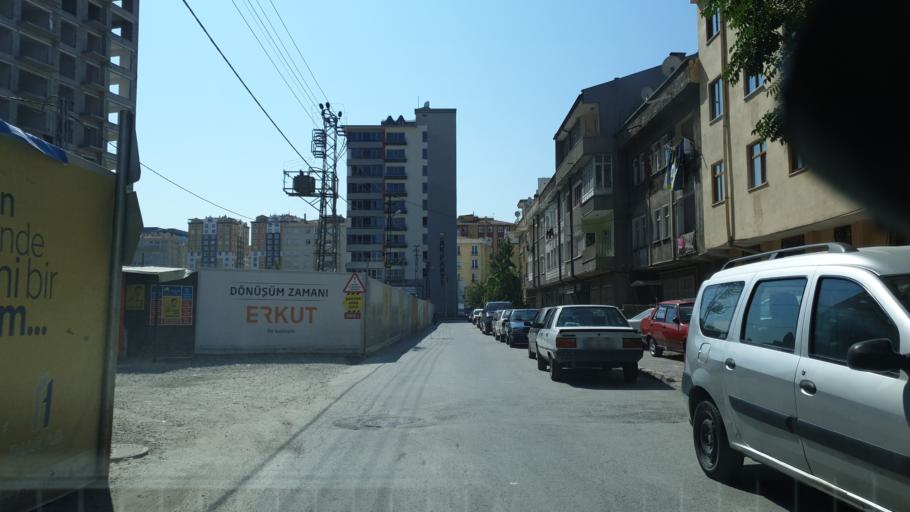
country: TR
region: Kayseri
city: Kayseri
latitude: 38.7276
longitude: 35.4900
